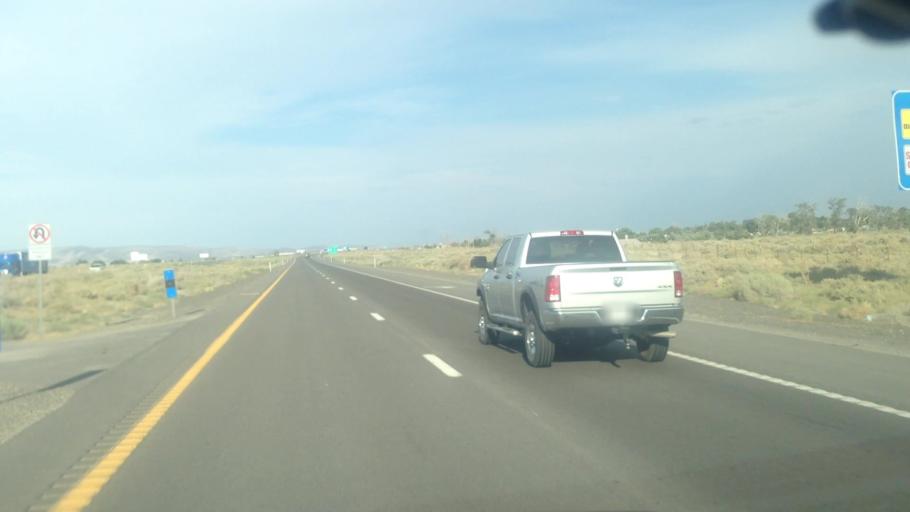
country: US
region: Nevada
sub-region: Lyon County
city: Fernley
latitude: 39.6150
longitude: -119.2497
